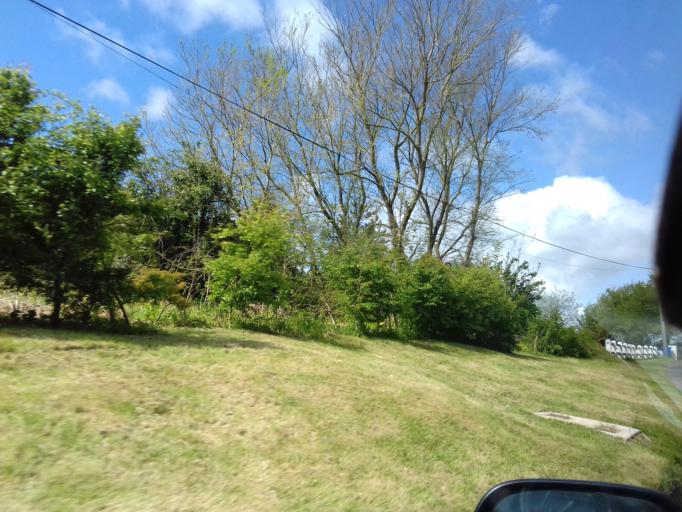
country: IE
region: Leinster
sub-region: Loch Garman
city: Castlebridge
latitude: 52.3899
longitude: -6.3802
